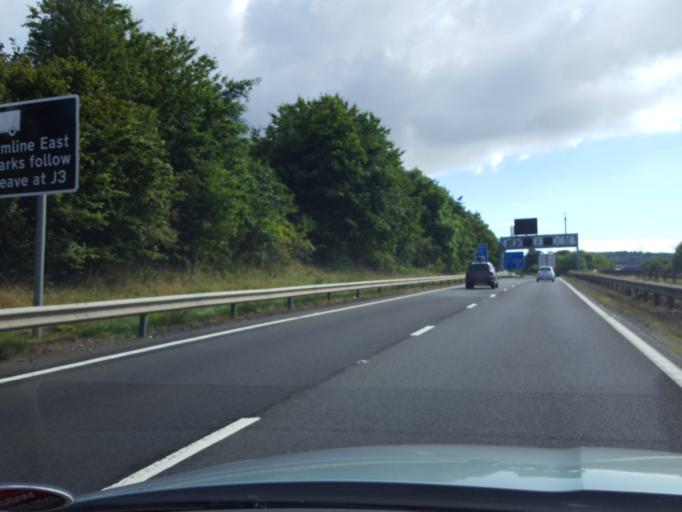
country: GB
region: Scotland
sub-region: Fife
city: Rosyth
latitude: 56.0459
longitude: -3.4158
